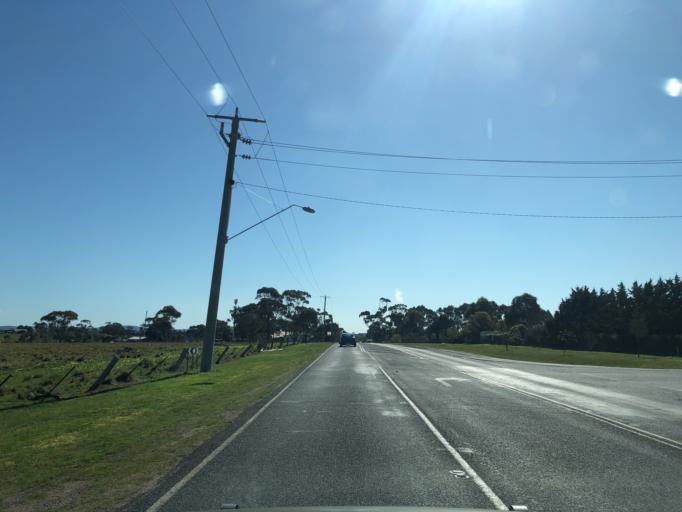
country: AU
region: Victoria
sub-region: Hume
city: Diggers Rest
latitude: -37.6334
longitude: 144.7253
